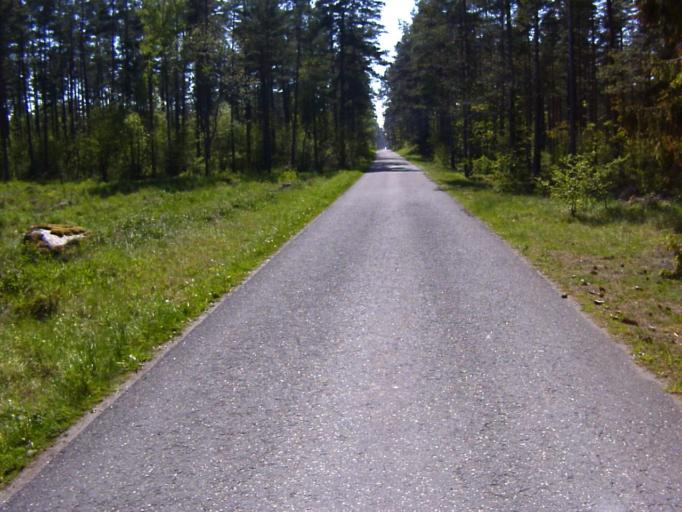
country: SE
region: Skane
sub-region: Kristianstads Kommun
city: Degeberga
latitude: 55.9116
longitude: 14.1052
